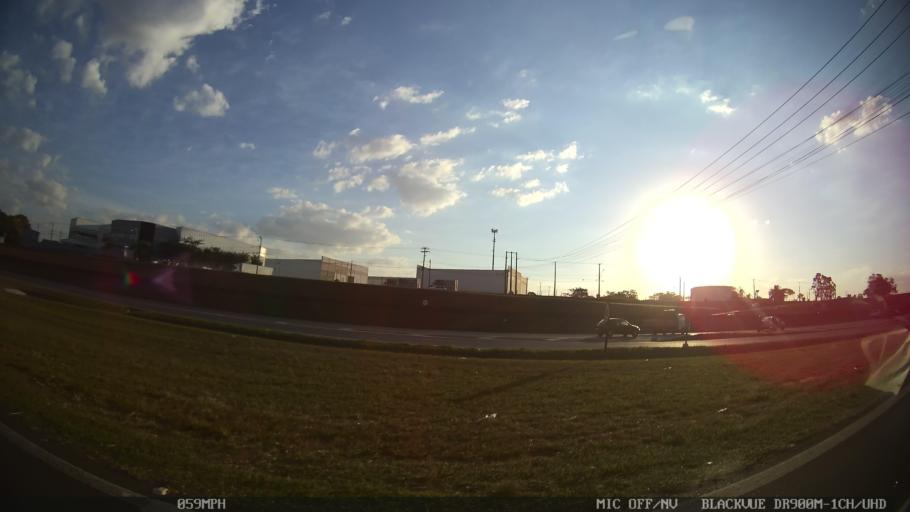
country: BR
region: Sao Paulo
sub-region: Ribeirao Preto
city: Ribeirao Preto
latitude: -21.1518
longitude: -47.7571
